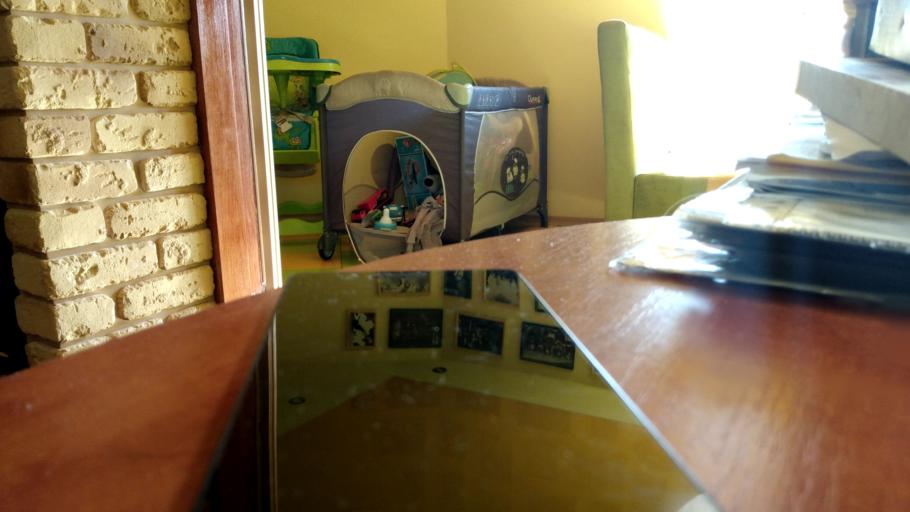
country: RU
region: Penza
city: Serdobsk
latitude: 52.4540
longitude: 44.2896
